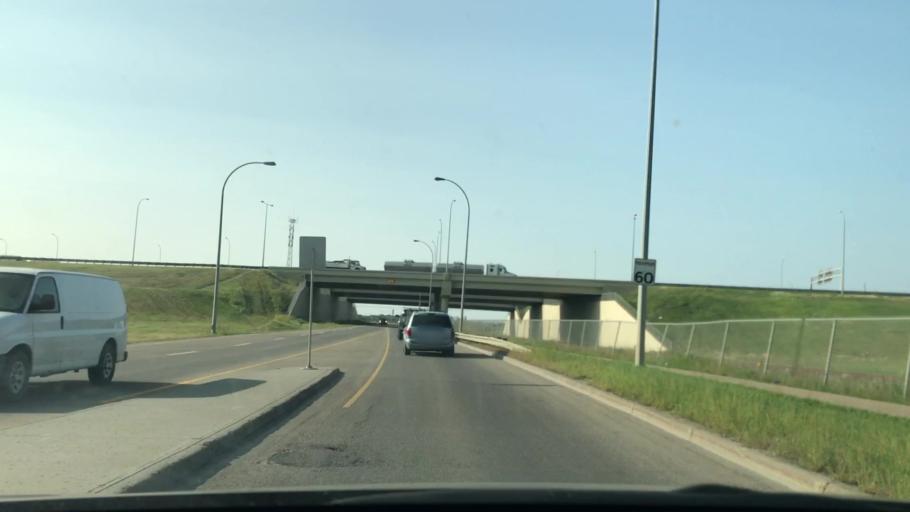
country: CA
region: Alberta
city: Beaumont
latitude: 53.4393
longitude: -113.4843
